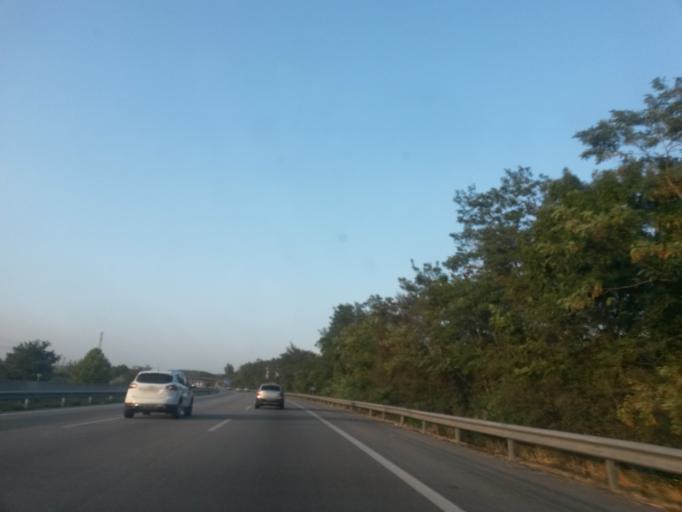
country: ES
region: Catalonia
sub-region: Provincia de Barcelona
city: Llinars del Valles
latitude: 41.6395
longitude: 2.4122
